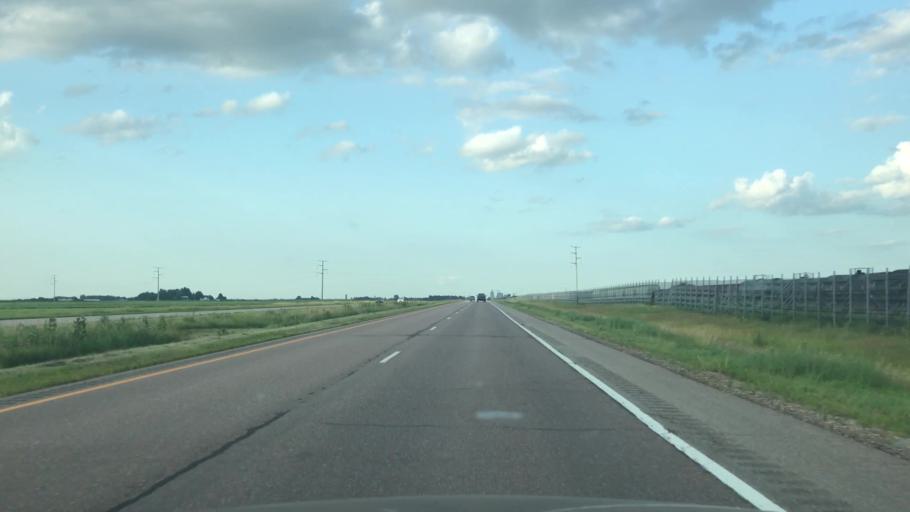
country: US
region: Minnesota
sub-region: Nobles County
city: Worthington
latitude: 43.6674
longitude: -95.5196
